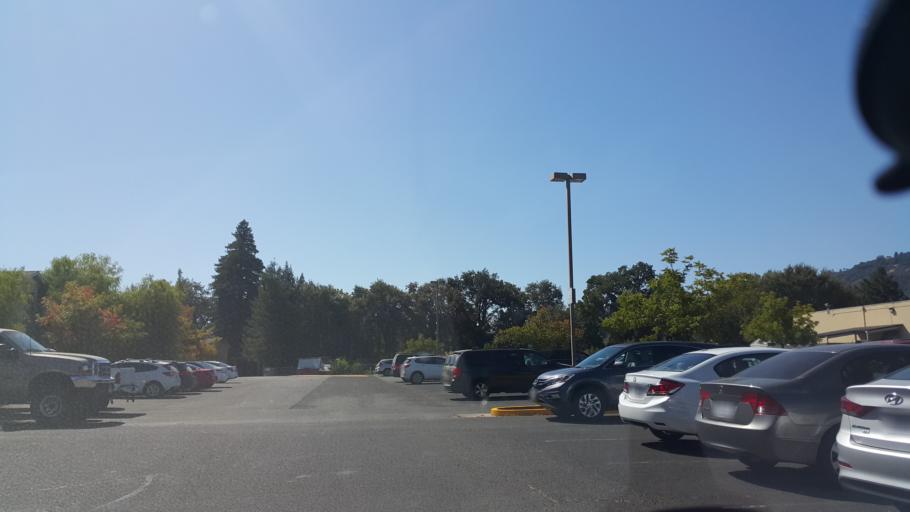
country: US
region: California
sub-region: Mendocino County
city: Ukiah
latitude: 39.1422
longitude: -123.2040
